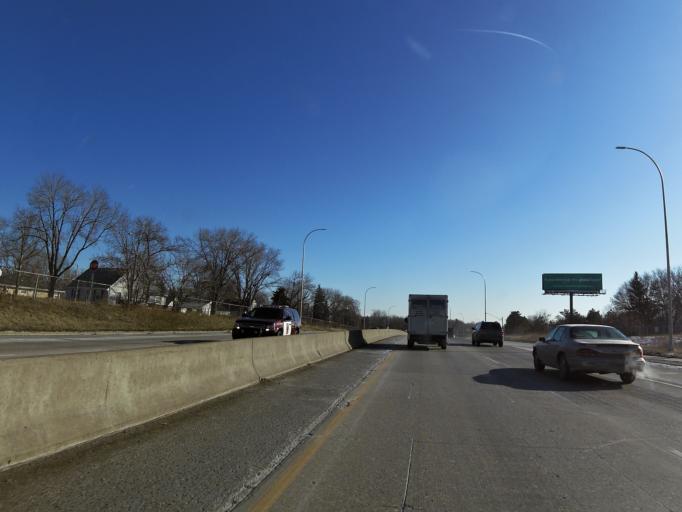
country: US
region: Minnesota
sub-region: Hennepin County
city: Richfield
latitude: 44.8978
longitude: -93.2209
